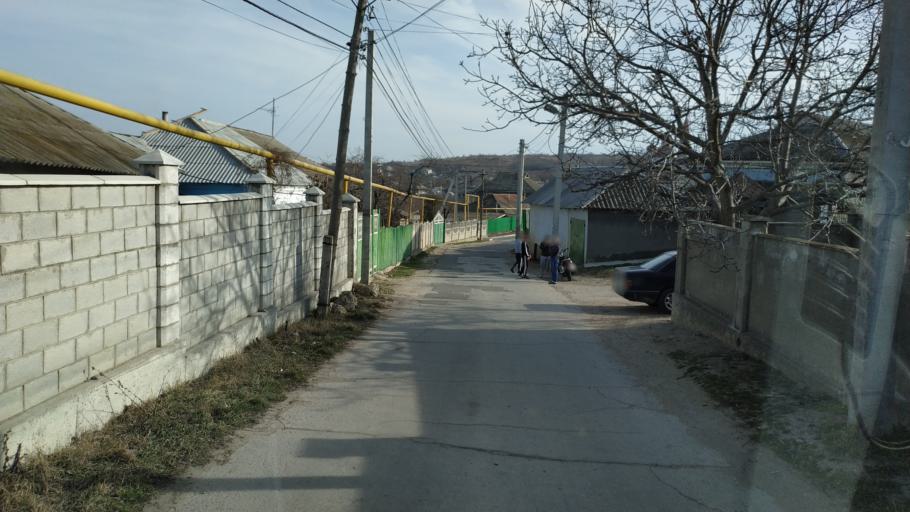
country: MD
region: Chisinau
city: Vatra
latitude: 47.0701
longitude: 28.6738
